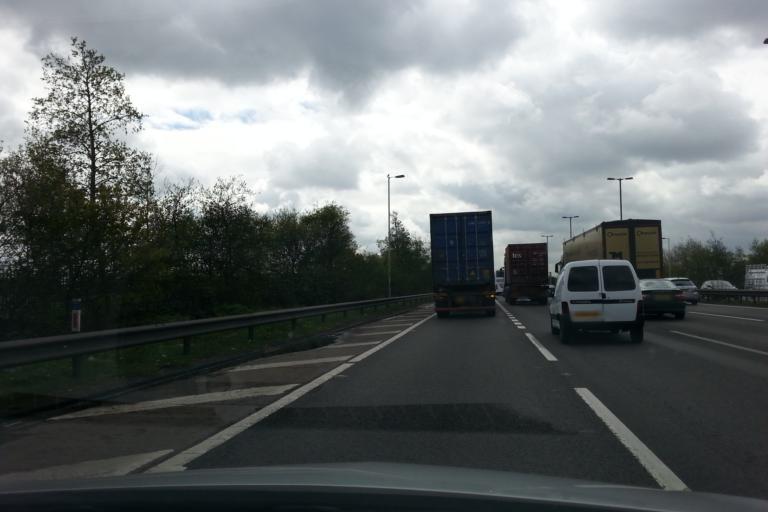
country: GB
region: England
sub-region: Walsall
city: Darlaston
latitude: 52.5792
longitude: -2.0136
